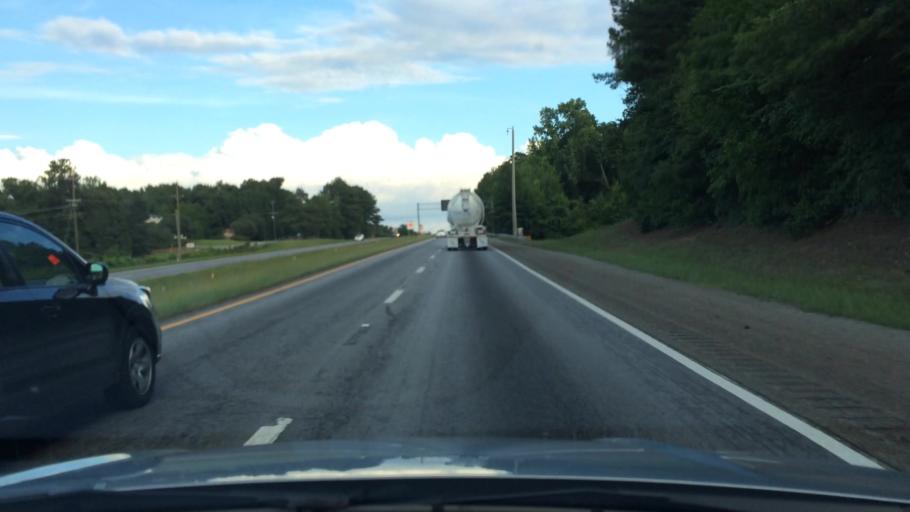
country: US
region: South Carolina
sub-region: Lexington County
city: Irmo
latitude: 34.1108
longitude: -81.1872
